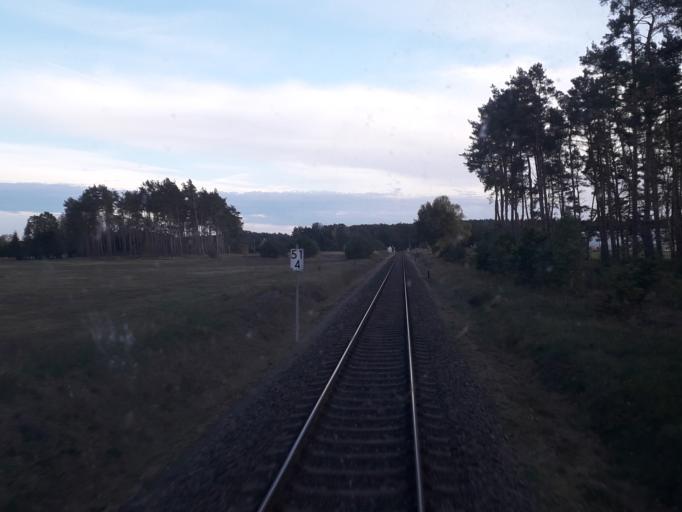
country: DE
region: Brandenburg
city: Wittstock
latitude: 53.0464
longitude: 12.5595
